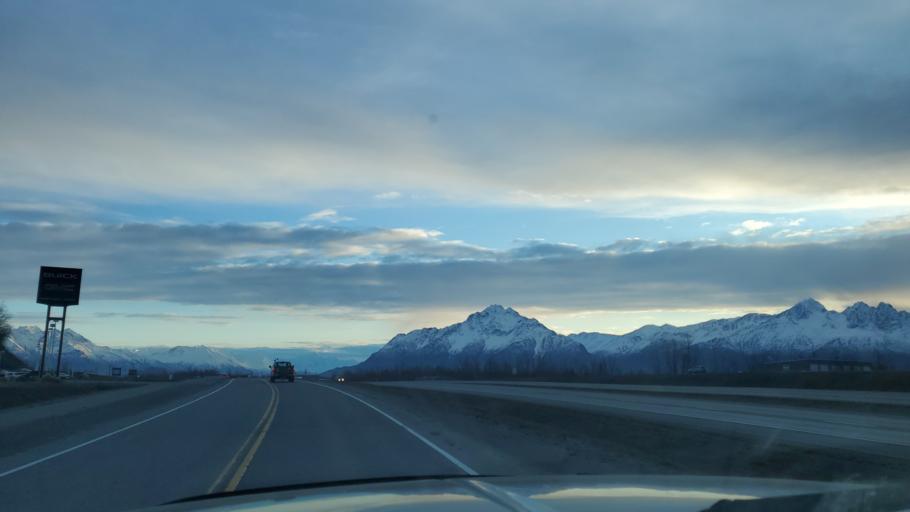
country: US
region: Alaska
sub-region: Matanuska-Susitna Borough
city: Lakes
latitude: 61.5638
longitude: -149.3013
